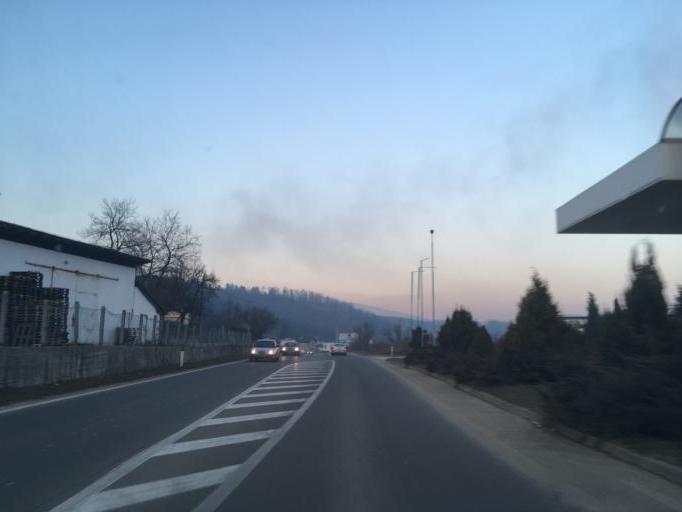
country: BA
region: Federation of Bosnia and Herzegovina
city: Novi Travnik
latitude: 44.1837
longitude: 17.6711
